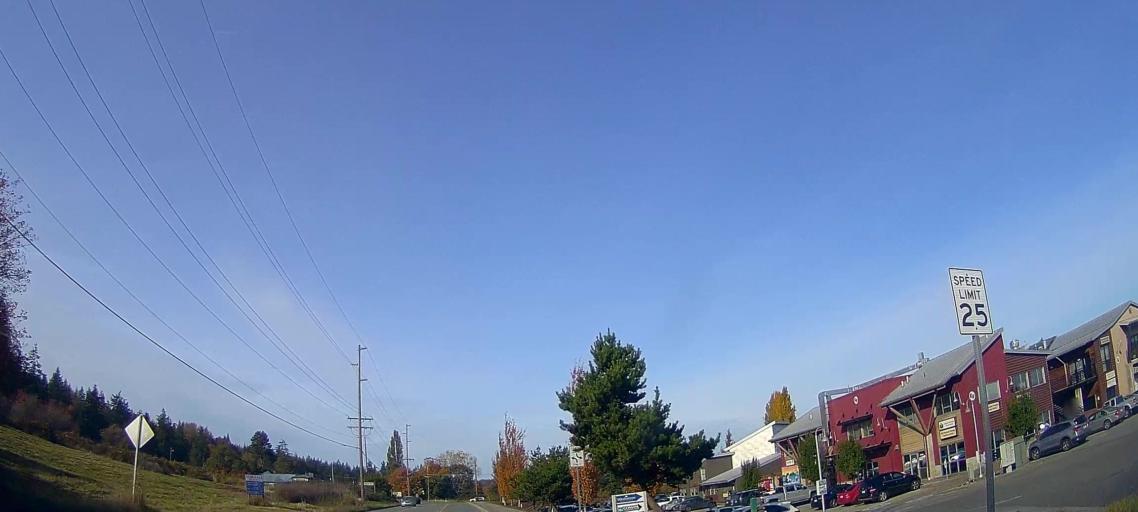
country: US
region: Washington
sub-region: Snohomish County
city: Stanwood
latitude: 48.2408
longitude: -122.4557
